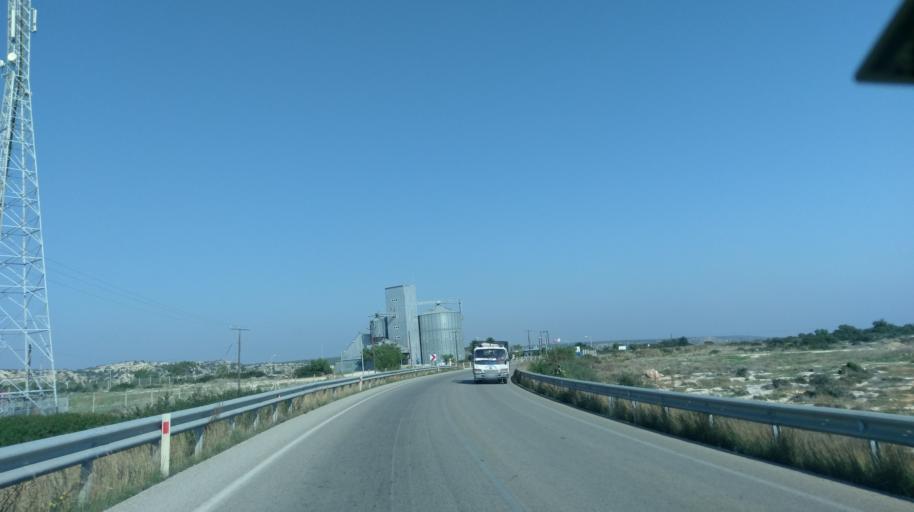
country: CY
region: Ammochostos
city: Leonarisso
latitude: 35.4322
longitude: 34.1282
